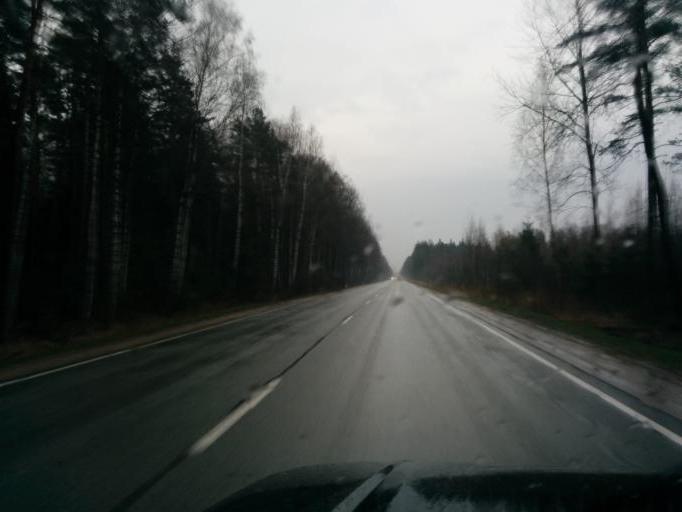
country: LV
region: Kekava
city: Balozi
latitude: 56.8161
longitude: 24.1280
